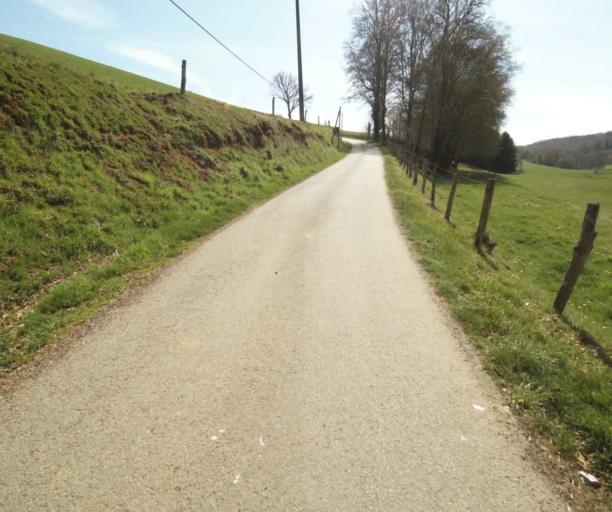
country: FR
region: Limousin
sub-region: Departement de la Correze
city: Seilhac
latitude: 45.3881
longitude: 1.7763
